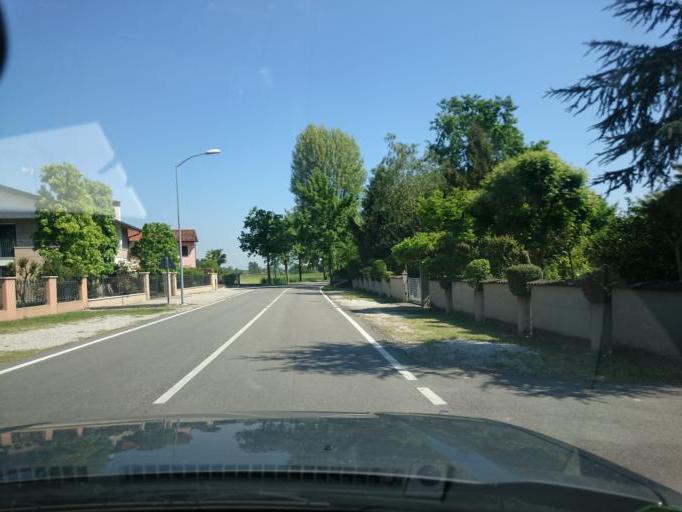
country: IT
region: Veneto
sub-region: Provincia di Venezia
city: Noale
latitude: 45.5378
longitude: 12.0569
